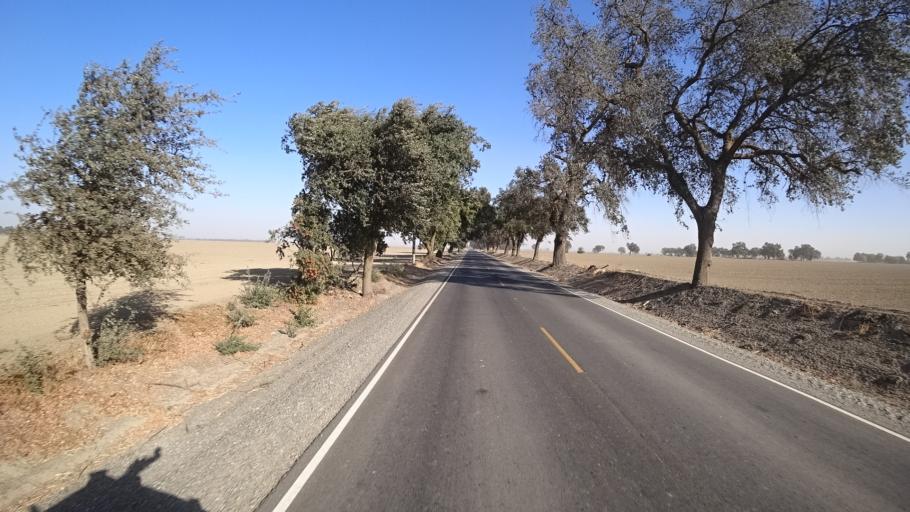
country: US
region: California
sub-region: Yolo County
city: Woodland
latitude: 38.7939
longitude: -121.8438
